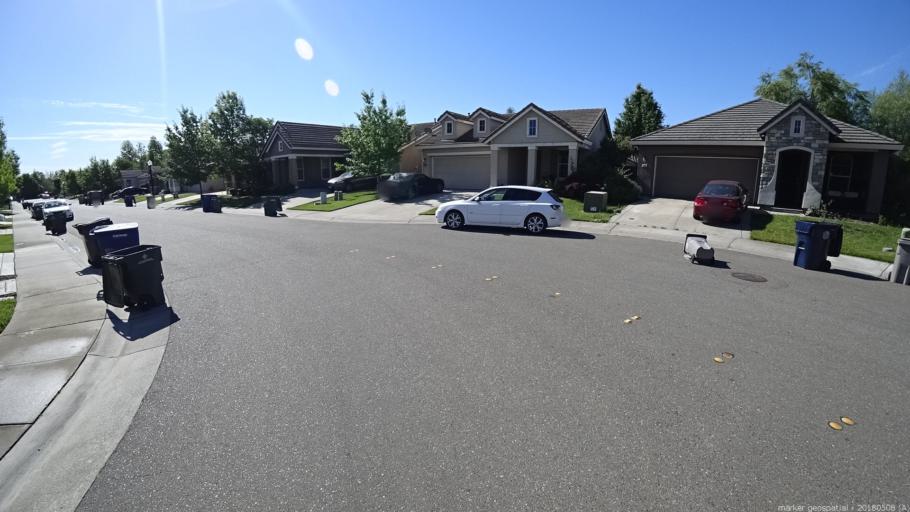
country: US
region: California
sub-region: Sacramento County
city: Elverta
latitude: 38.6828
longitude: -121.4997
